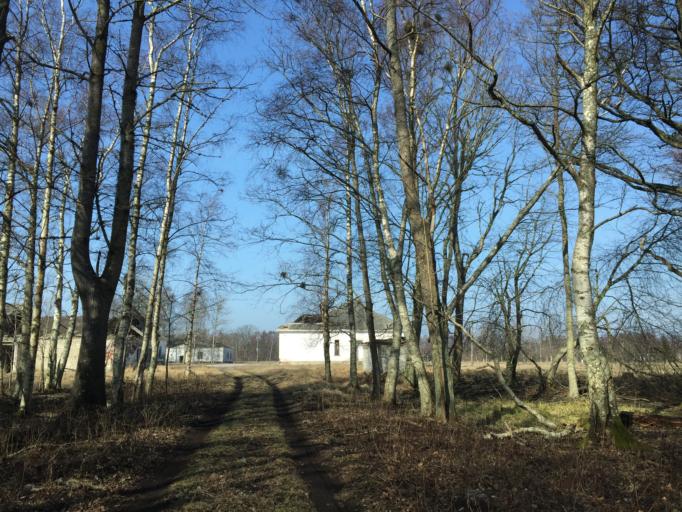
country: LV
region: Dundaga
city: Dundaga
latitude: 57.9343
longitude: 22.0710
